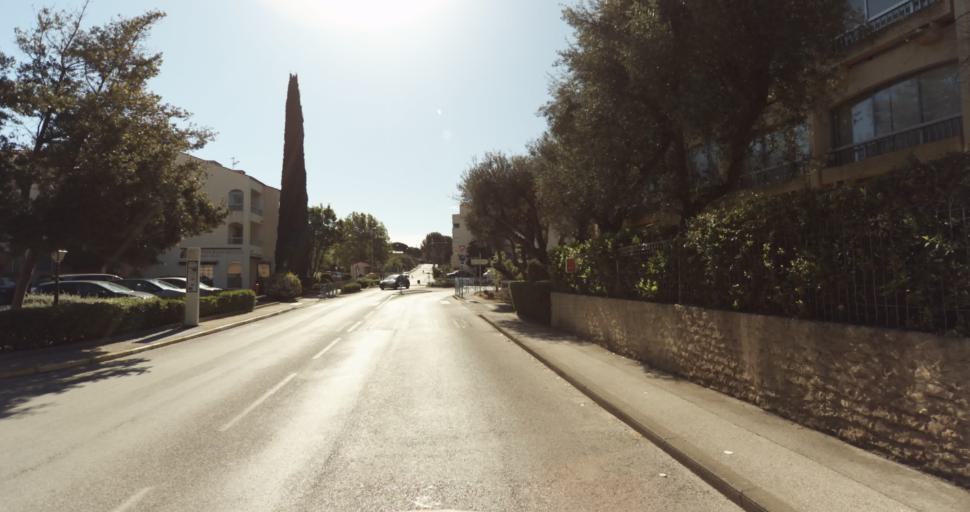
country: FR
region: Provence-Alpes-Cote d'Azur
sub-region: Departement du Var
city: Saint-Mandrier-sur-Mer
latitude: 43.0750
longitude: 5.9079
